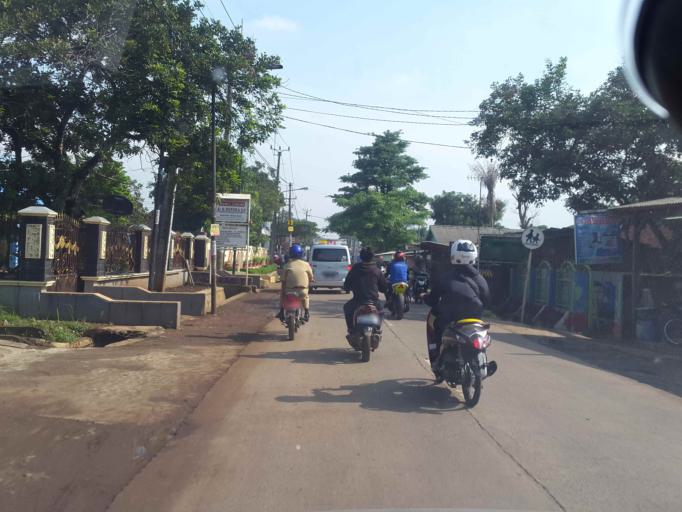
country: ID
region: West Java
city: Cileungsir
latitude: -6.3434
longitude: 107.0371
